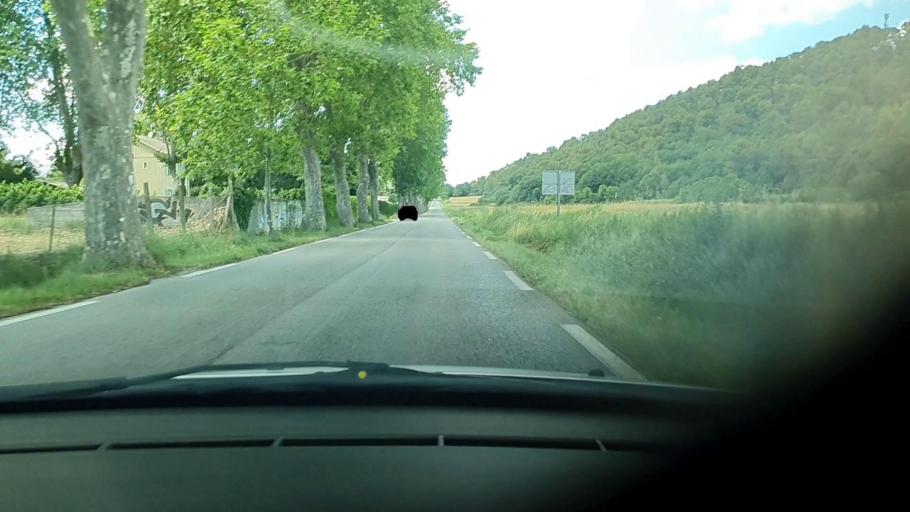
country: FR
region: Languedoc-Roussillon
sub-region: Departement du Gard
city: Montaren-et-Saint-Mediers
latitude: 44.0316
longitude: 4.3712
